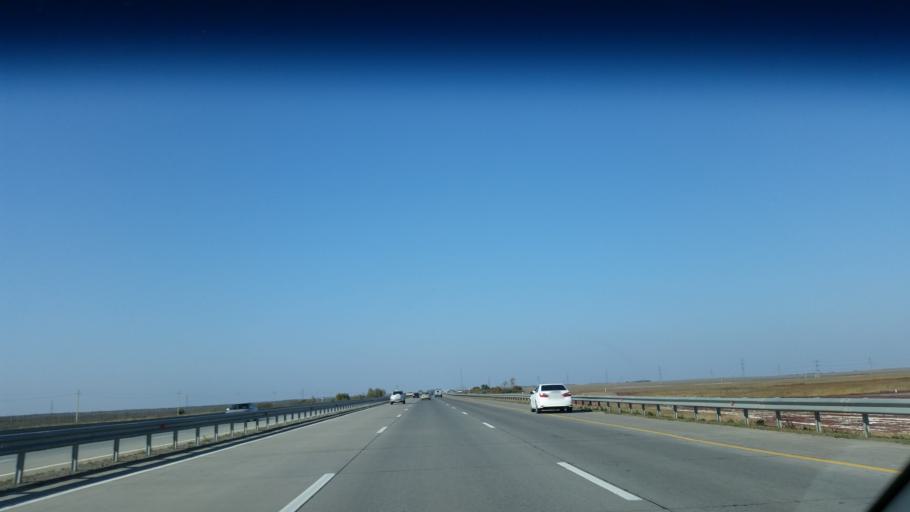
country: KZ
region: Astana Qalasy
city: Astana
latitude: 51.2752
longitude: 71.3657
